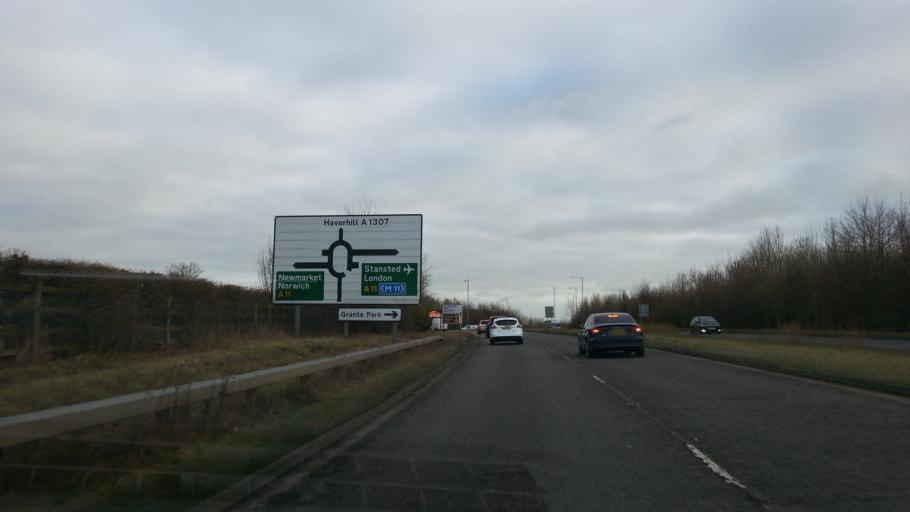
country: GB
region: England
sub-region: Cambridgeshire
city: Sawston
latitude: 52.1303
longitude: 0.2192
